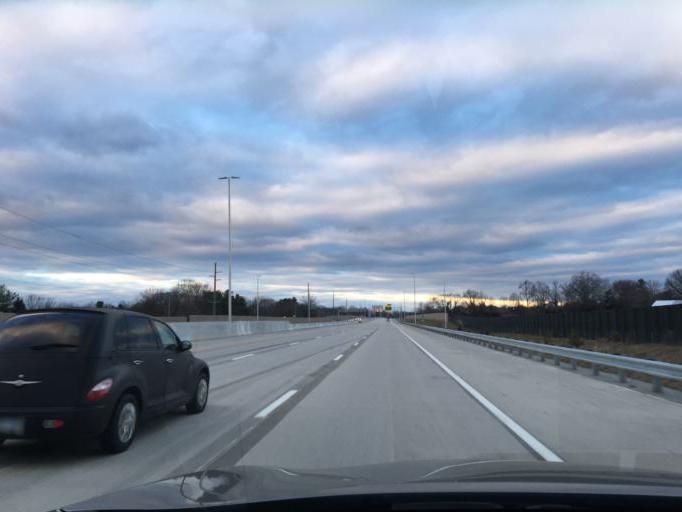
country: US
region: Kentucky
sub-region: Jefferson County
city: Barbourmeade
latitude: 38.3183
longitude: -85.5999
